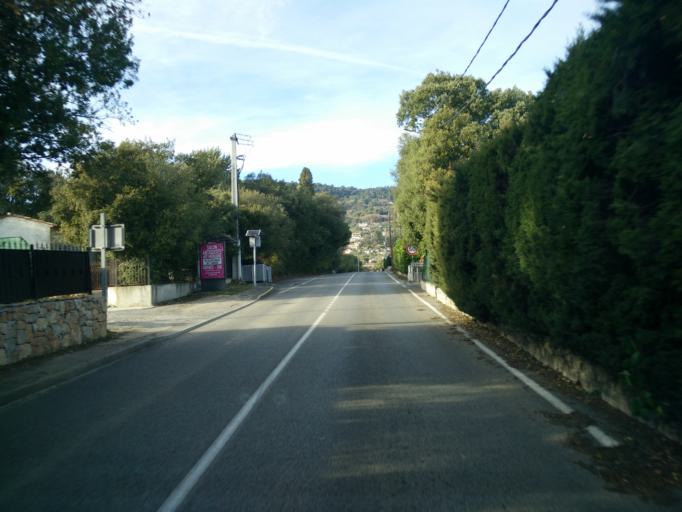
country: FR
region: Provence-Alpes-Cote d'Azur
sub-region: Departement des Alpes-Maritimes
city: Speracedes
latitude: 43.6377
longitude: 6.8564
